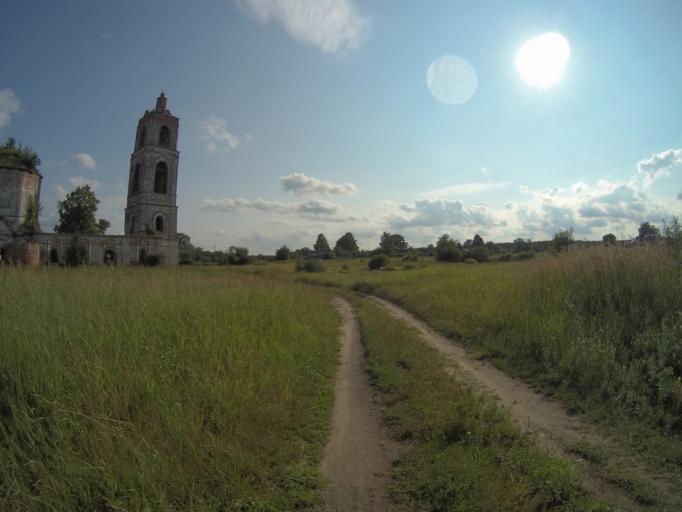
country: RU
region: Vladimir
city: Orgtrud
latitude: 56.3427
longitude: 40.6916
